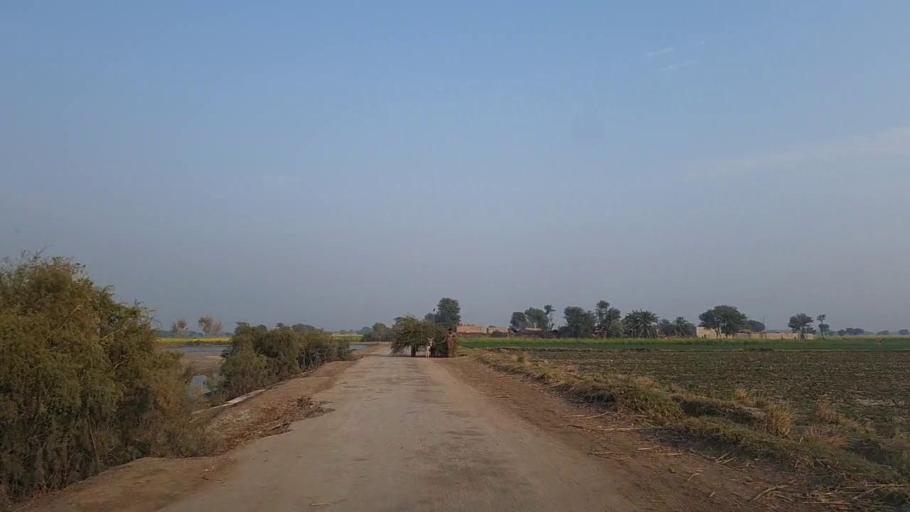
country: PK
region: Sindh
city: Jam Sahib
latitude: 26.3206
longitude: 68.5867
